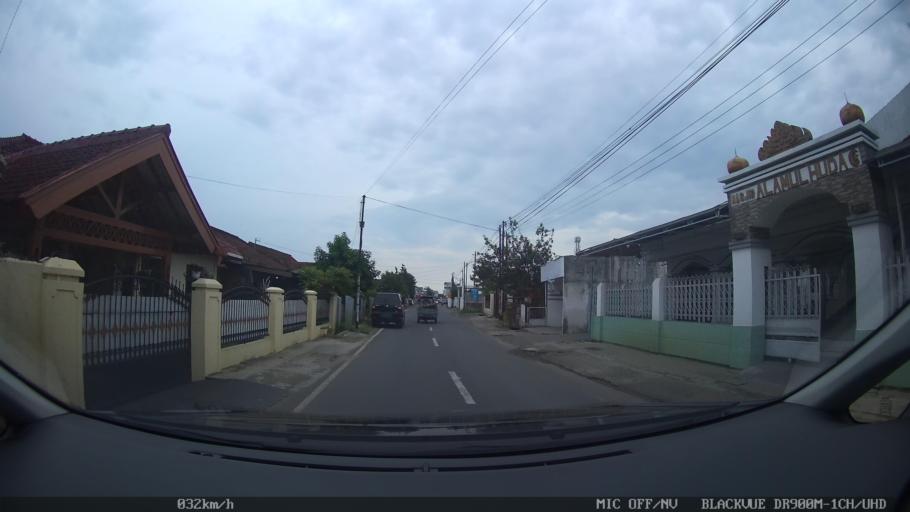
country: ID
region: Lampung
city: Kedaton
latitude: -5.3856
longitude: 105.2524
